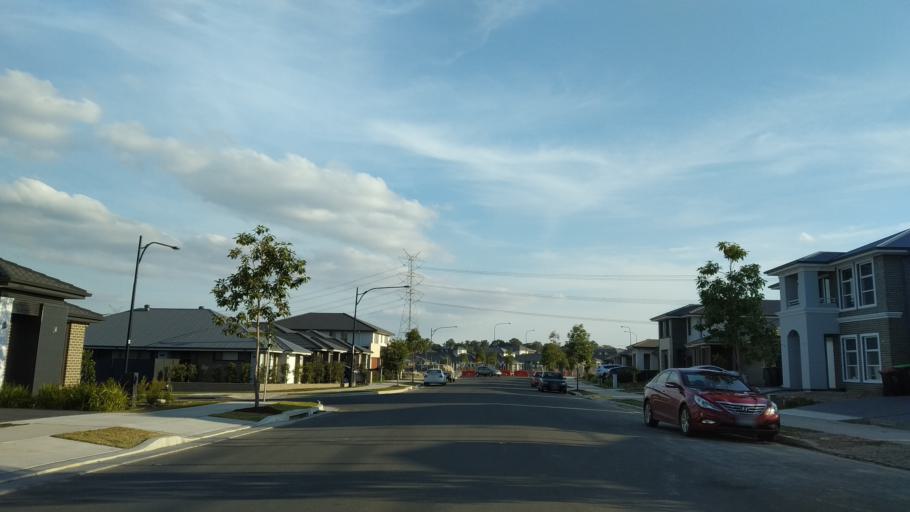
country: AU
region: New South Wales
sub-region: Penrith Municipality
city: Werrington County
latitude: -33.7364
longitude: 150.7528
